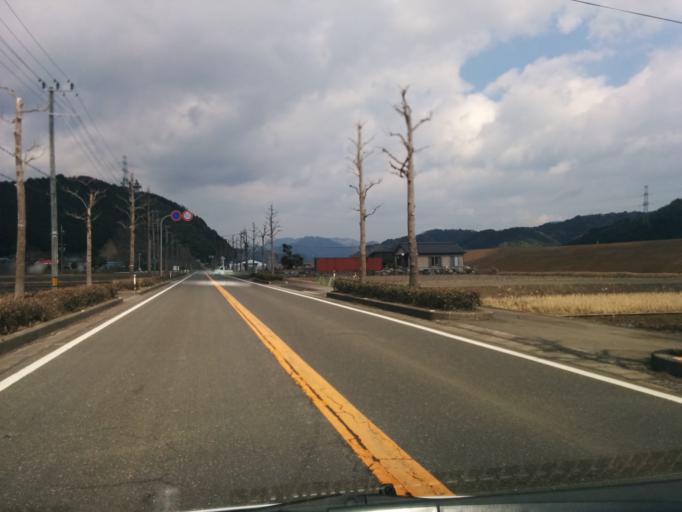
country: JP
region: Kyoto
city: Maizuru
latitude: 35.4344
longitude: 135.2533
